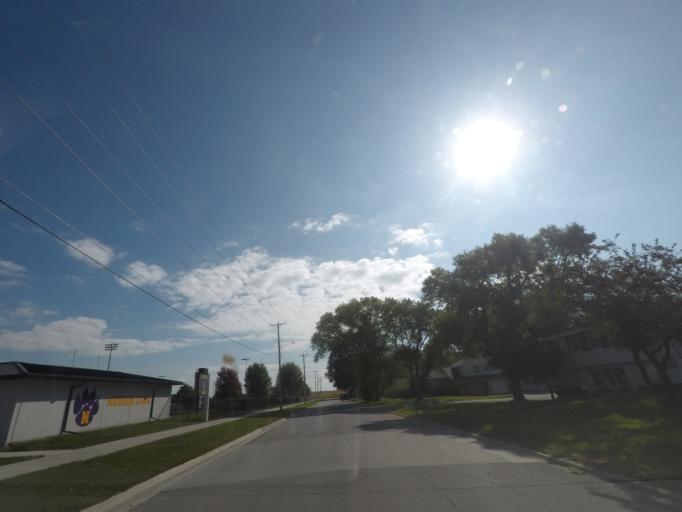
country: US
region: Iowa
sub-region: Story County
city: Nevada
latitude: 42.0192
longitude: -93.4379
